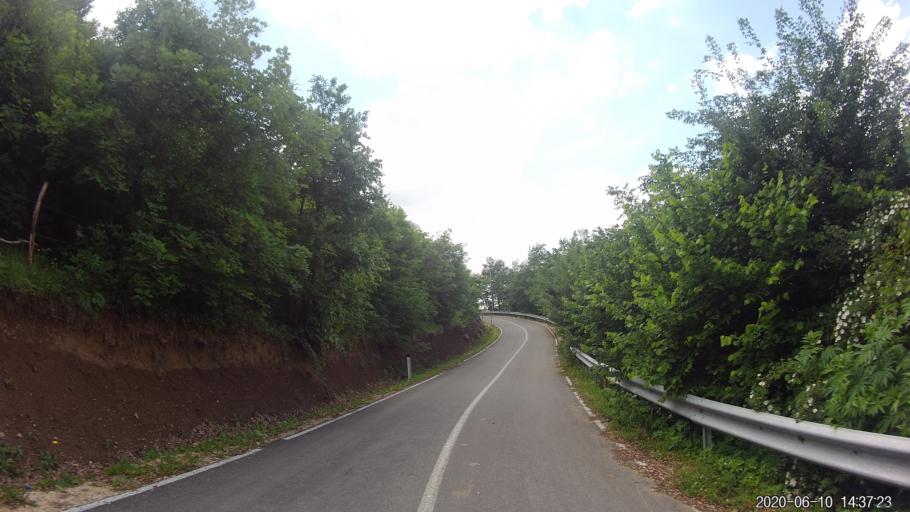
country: XK
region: Prizren
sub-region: Komuna e Therandes
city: Budakovo
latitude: 42.4088
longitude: 20.9403
